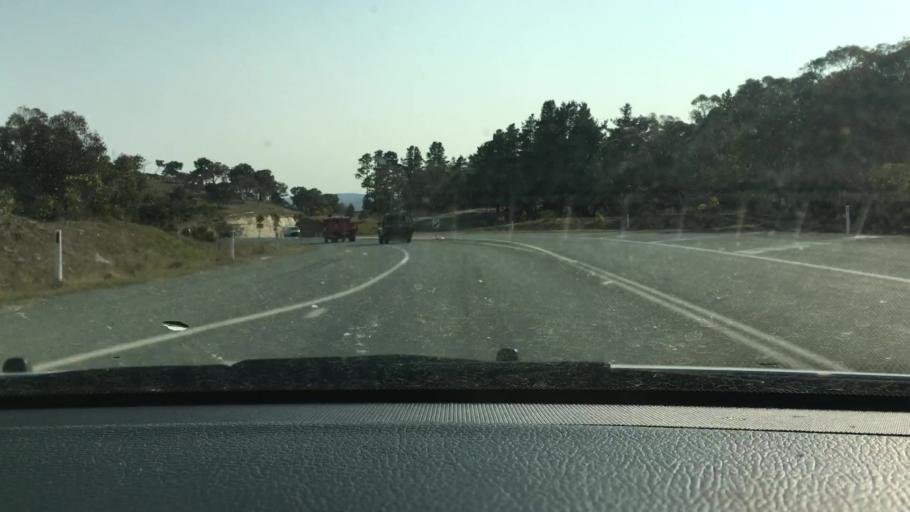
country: AU
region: New South Wales
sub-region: Queanbeyan
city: Queanbeyan
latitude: -35.4028
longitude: 149.2302
